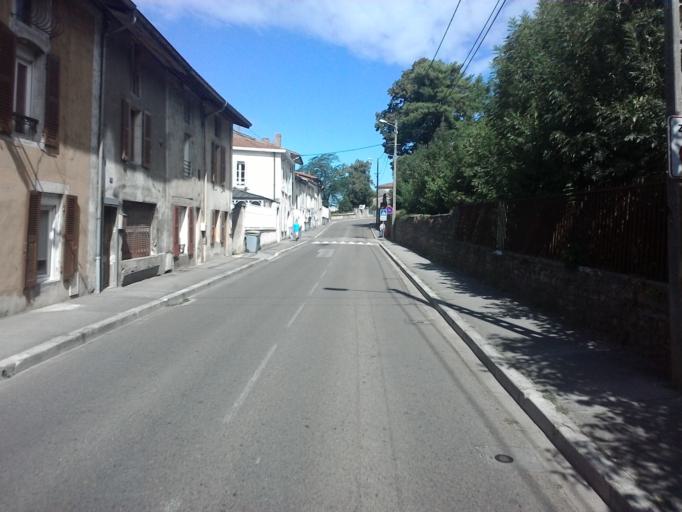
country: FR
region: Rhone-Alpes
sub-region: Departement de l'Ain
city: Amberieu-en-Bugey
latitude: 45.9561
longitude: 5.3609
